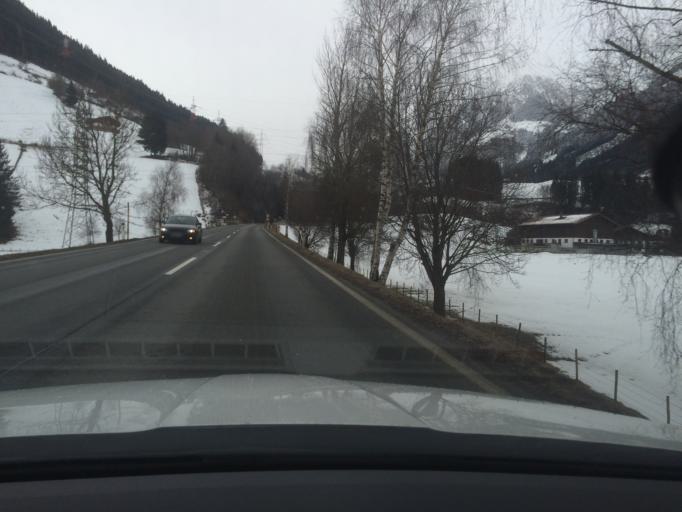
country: AT
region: Salzburg
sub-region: Politischer Bezirk Zell am See
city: Mittersill
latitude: 47.2757
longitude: 12.4878
